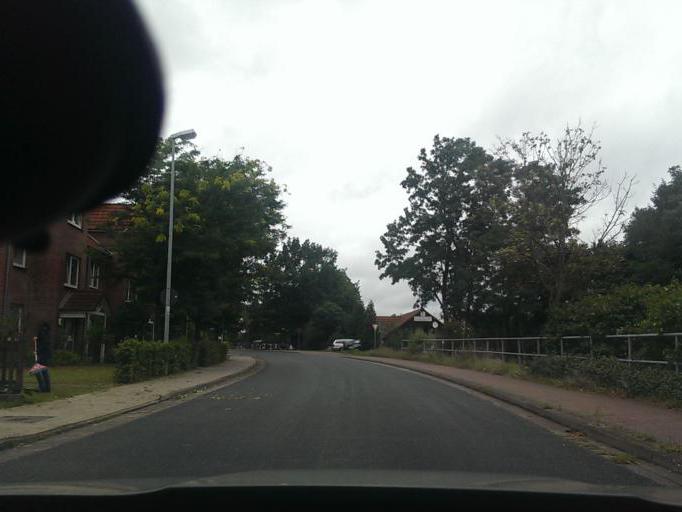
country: DE
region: Lower Saxony
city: Elze
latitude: 52.5489
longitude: 9.7435
